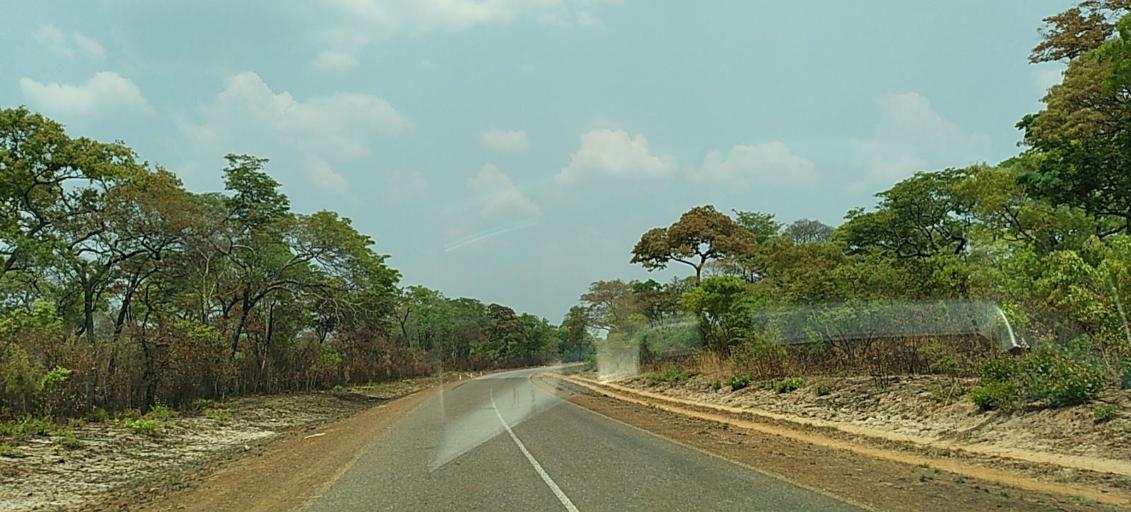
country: ZM
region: North-Western
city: Zambezi
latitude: -13.5585
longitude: 23.2090
